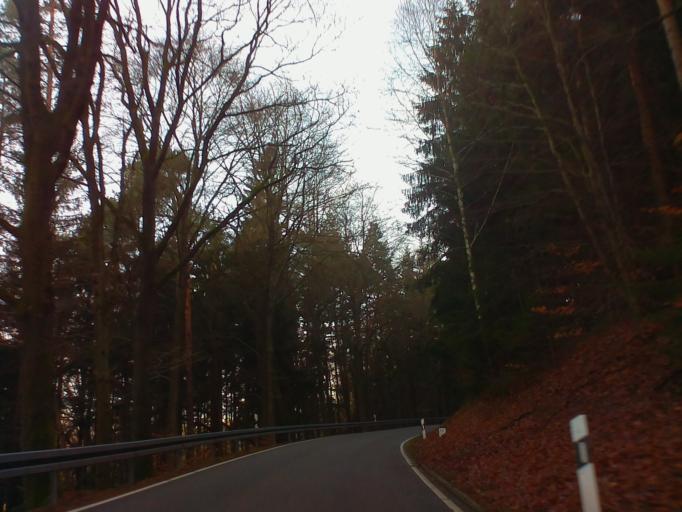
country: DE
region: Hesse
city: Reichelsheim
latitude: 49.6765
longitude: 8.8916
